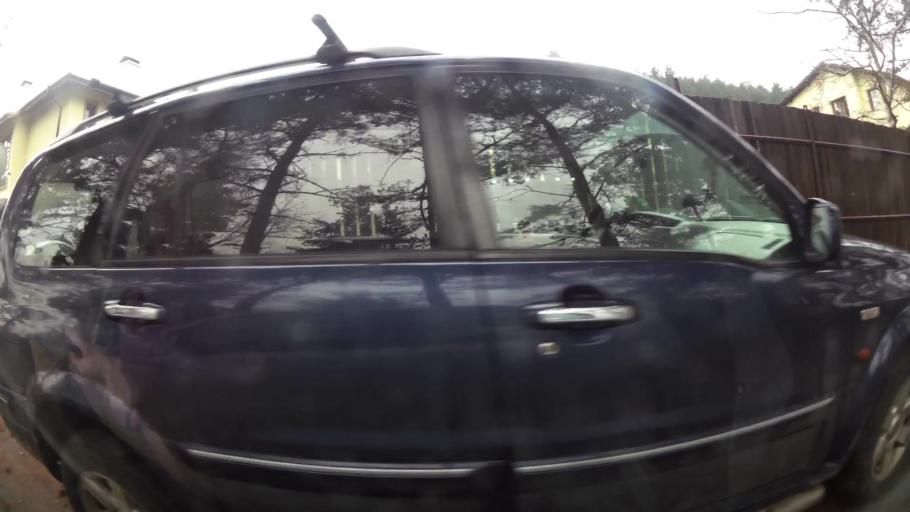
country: BG
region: Sofia-Capital
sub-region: Stolichna Obshtina
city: Sofia
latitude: 42.6081
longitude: 23.3610
